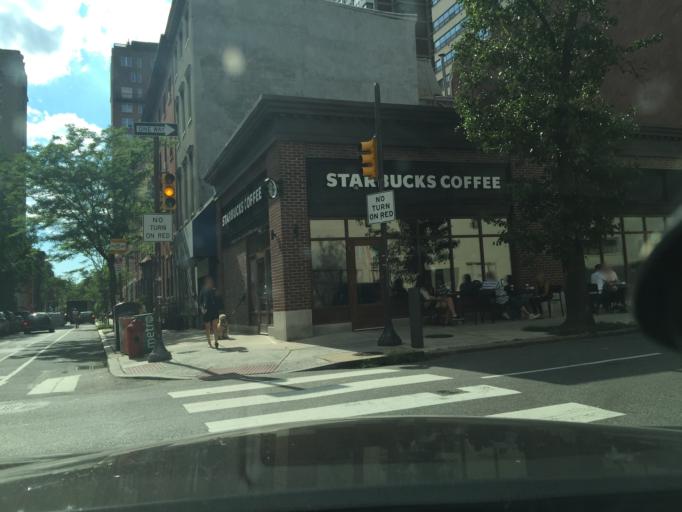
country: US
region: Pennsylvania
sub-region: Philadelphia County
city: Philadelphia
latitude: 39.9478
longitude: -75.1711
